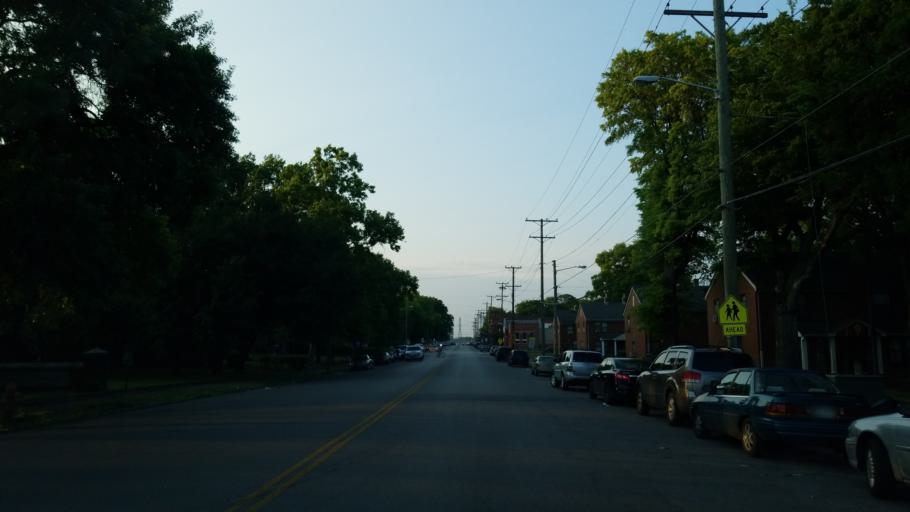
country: US
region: Tennessee
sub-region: Davidson County
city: Nashville
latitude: 36.1496
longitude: -86.7623
